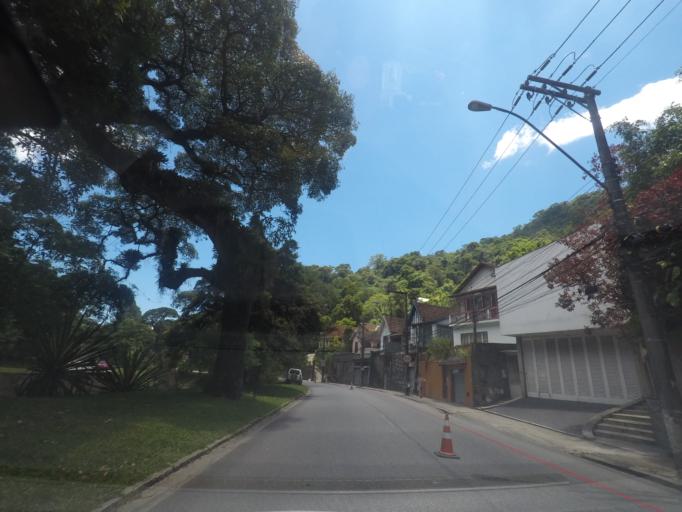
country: BR
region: Rio de Janeiro
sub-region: Petropolis
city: Petropolis
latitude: -22.5005
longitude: -43.1810
